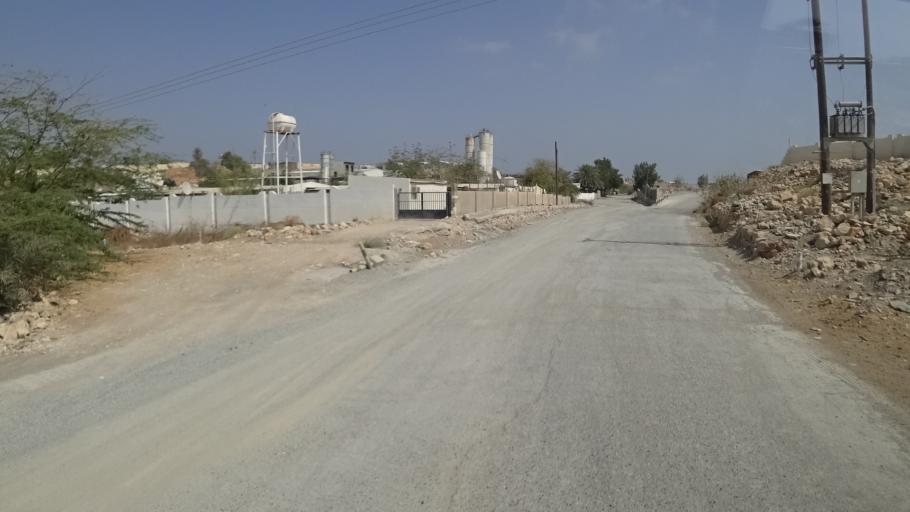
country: OM
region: Muhafazat Masqat
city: Bawshar
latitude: 23.5648
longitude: 58.3419
